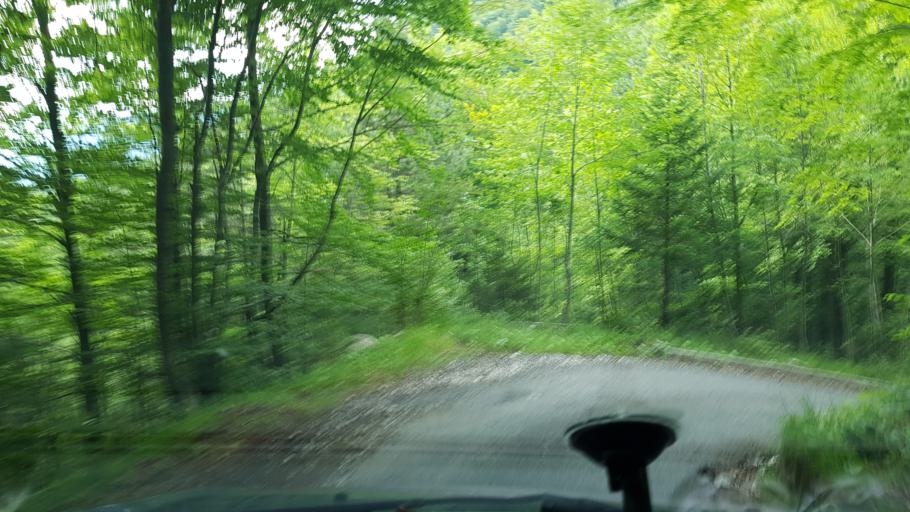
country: IT
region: Friuli Venezia Giulia
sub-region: Provincia di Udine
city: Prato
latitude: 46.3390
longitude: 13.4106
